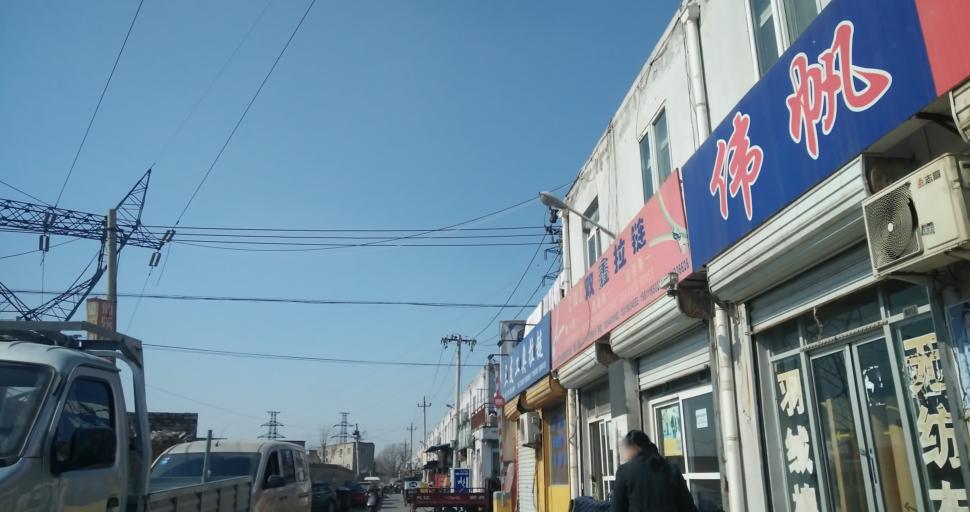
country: CN
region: Beijing
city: Dahongmen
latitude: 39.8211
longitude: 116.4130
